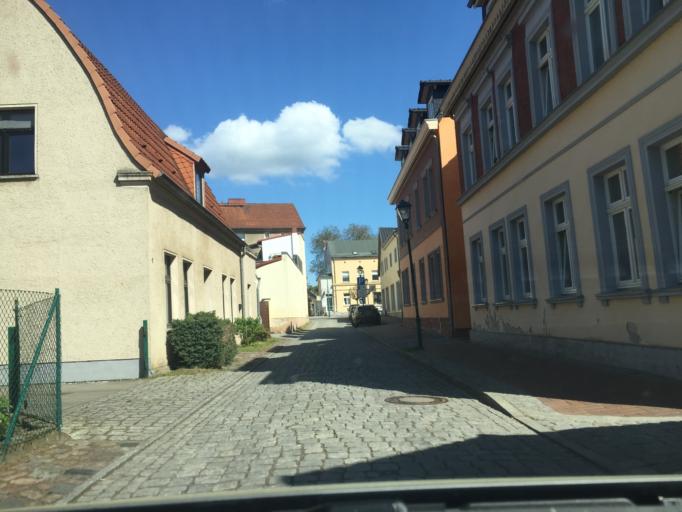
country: DE
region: Mecklenburg-Vorpommern
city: Torgelow
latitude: 53.6285
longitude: 14.0084
